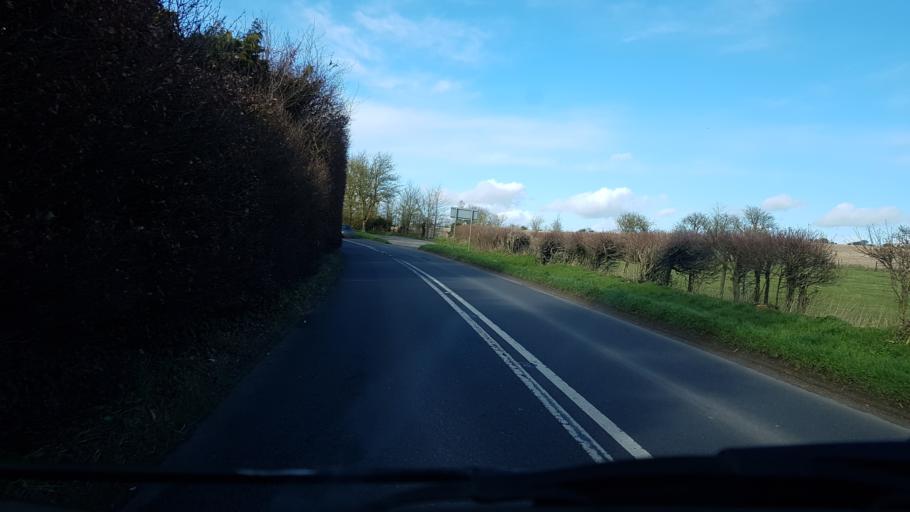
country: GB
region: England
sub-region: Wiltshire
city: Avebury
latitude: 51.4484
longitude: -1.8557
